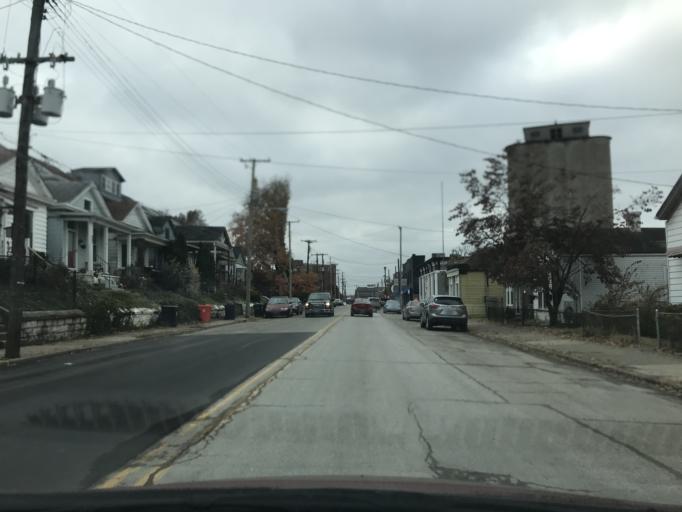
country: US
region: Kentucky
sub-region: Jefferson County
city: Louisville
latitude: 38.2465
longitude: -85.7316
